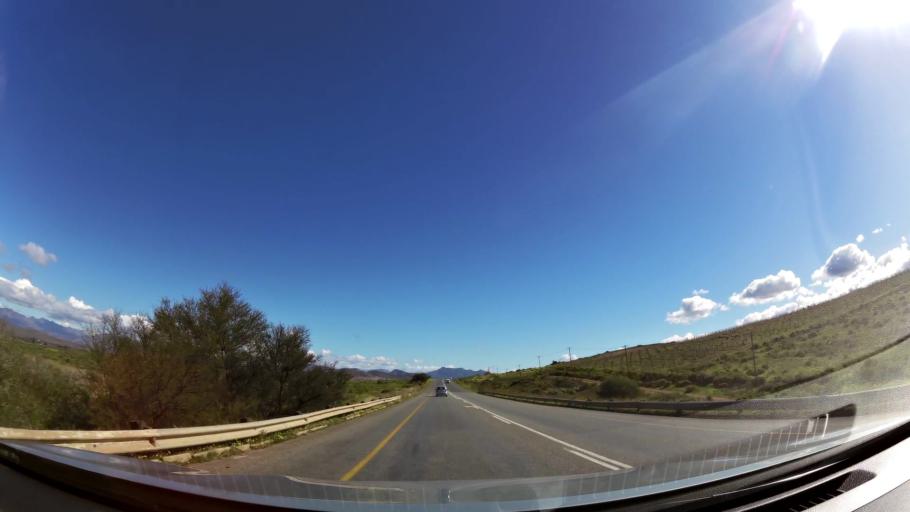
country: ZA
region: Western Cape
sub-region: Cape Winelands District Municipality
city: Ashton
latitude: -33.8179
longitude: 19.9545
